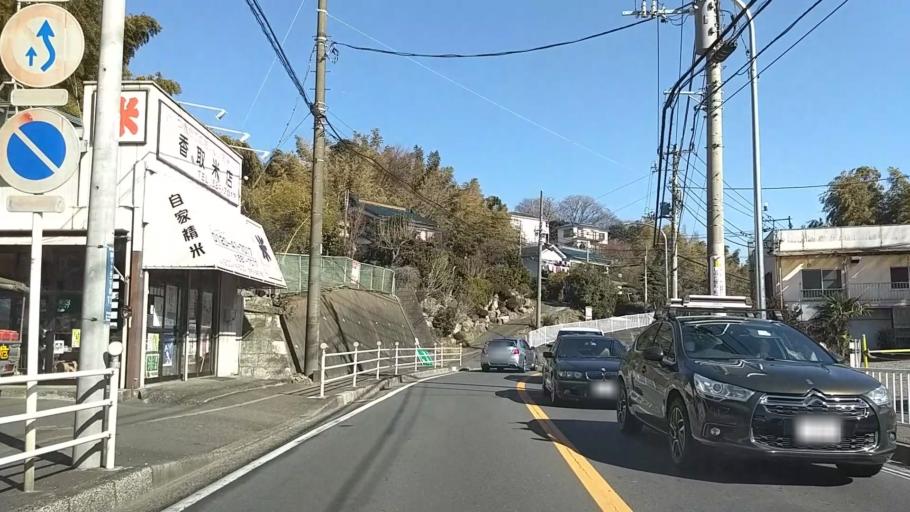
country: JP
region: Kanagawa
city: Yokohama
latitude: 35.5172
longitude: 139.6476
